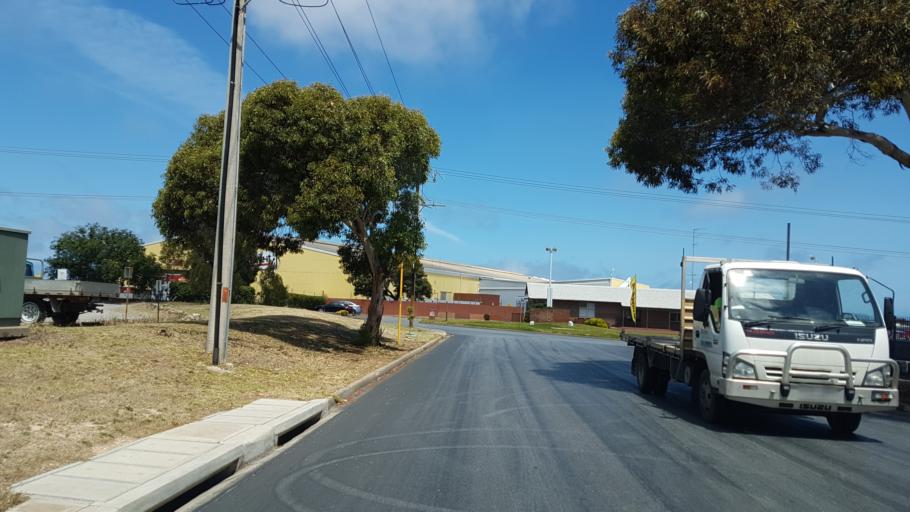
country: AU
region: South Australia
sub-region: Onkaparinga
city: Morphett Vale
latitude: -35.1135
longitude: 138.4976
